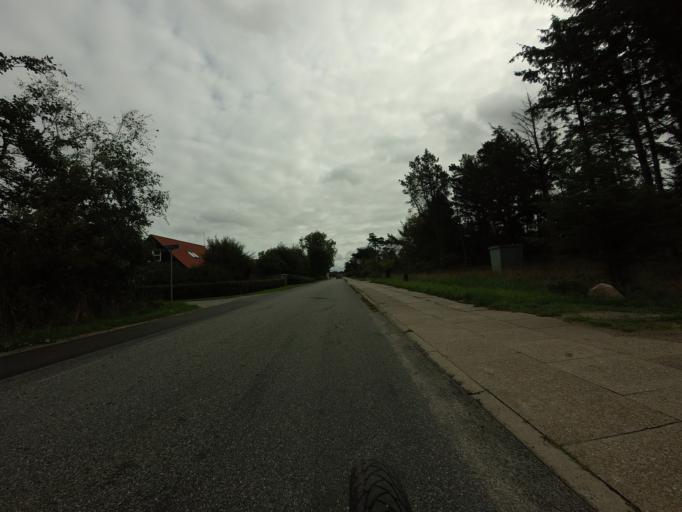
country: DK
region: North Denmark
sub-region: Hjorring Kommune
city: Hirtshals
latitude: 57.5556
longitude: 9.9297
